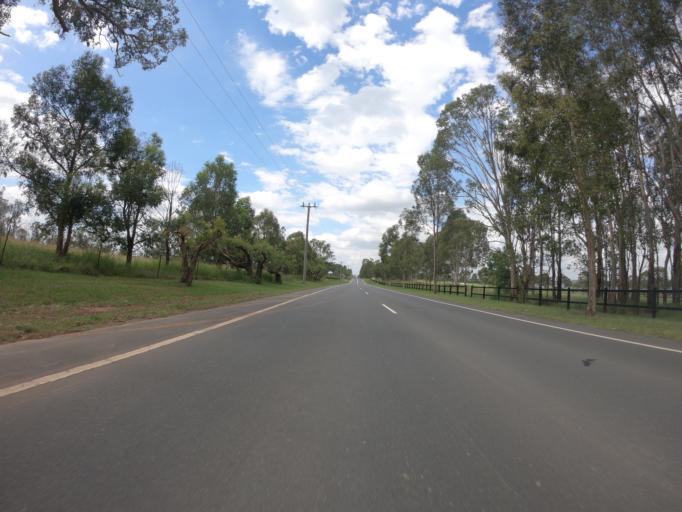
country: AU
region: New South Wales
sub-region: Liverpool
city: Luddenham
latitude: -33.8368
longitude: 150.7503
